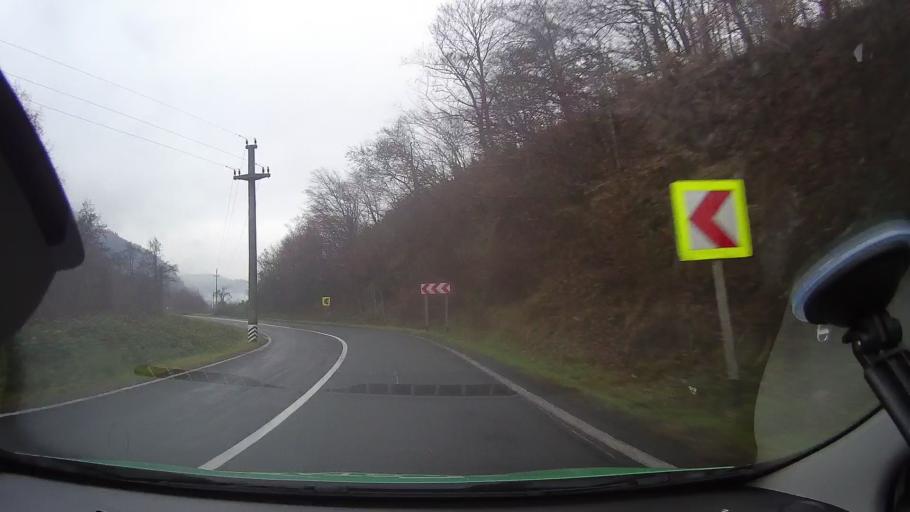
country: RO
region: Arad
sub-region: Comuna Plescuta
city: Plescuta
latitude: 46.3021
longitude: 22.4562
